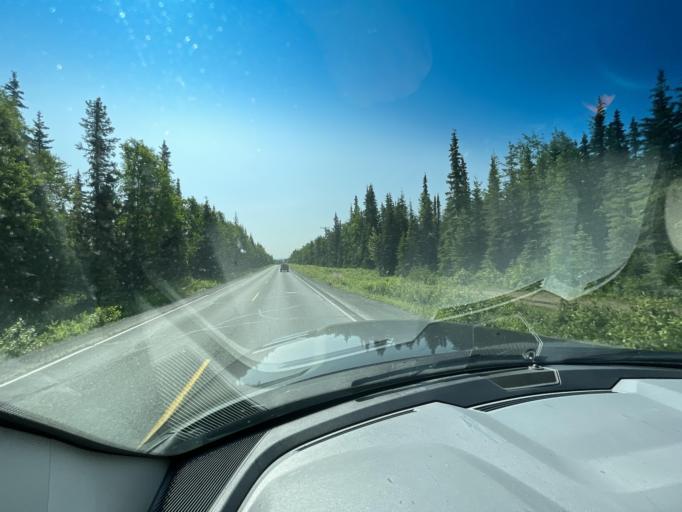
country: US
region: Alaska
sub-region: Kenai Peninsula Borough
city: Cohoe
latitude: 60.3072
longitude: -151.2887
